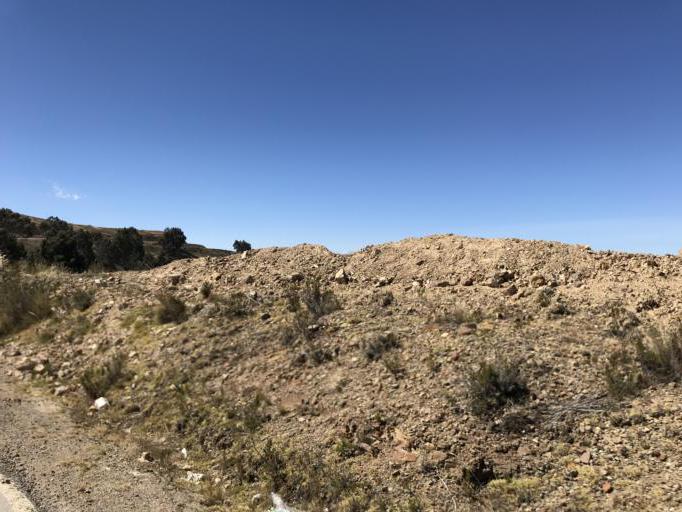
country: BO
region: La Paz
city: San Pablo
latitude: -16.2004
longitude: -68.8312
